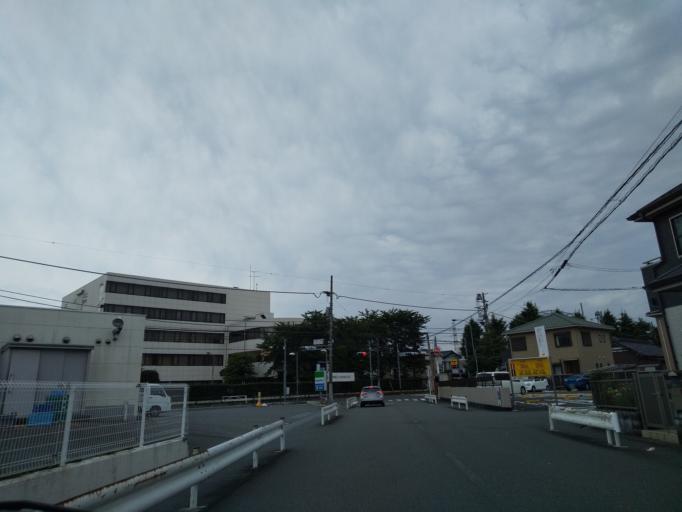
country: JP
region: Tokyo
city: Hino
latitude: 35.6694
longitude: 139.3710
